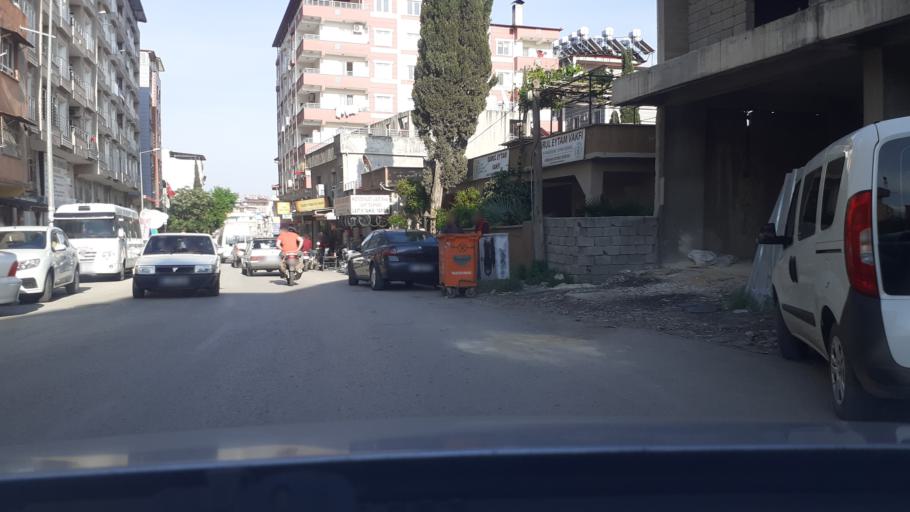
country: TR
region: Hatay
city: Kirikhan
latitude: 36.4968
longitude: 36.3581
